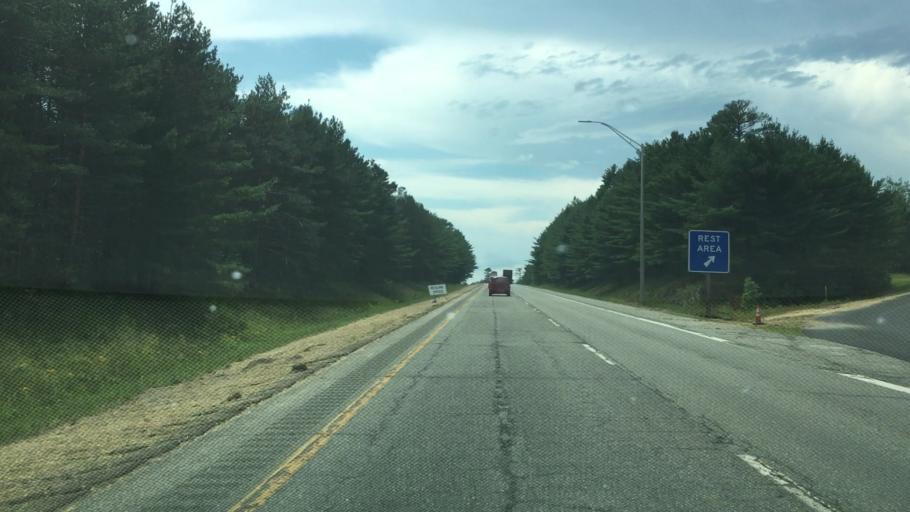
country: US
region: Maine
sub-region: Penobscot County
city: Medway
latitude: 45.5983
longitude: -68.5343
